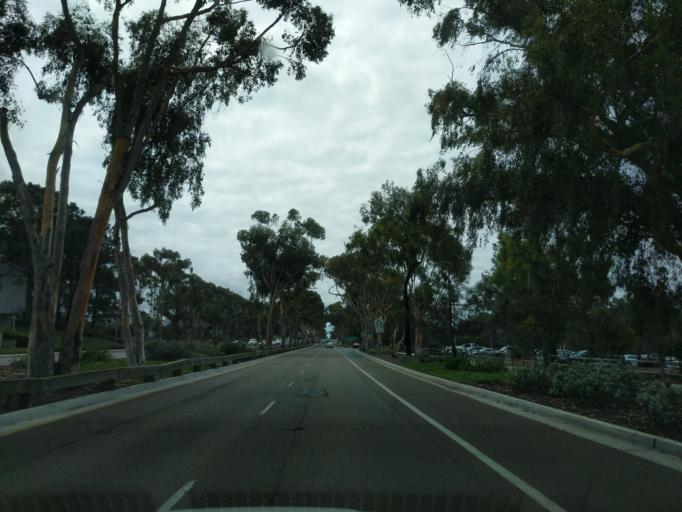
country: US
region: California
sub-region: San Diego County
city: Del Mar
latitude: 32.9064
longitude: -117.2438
